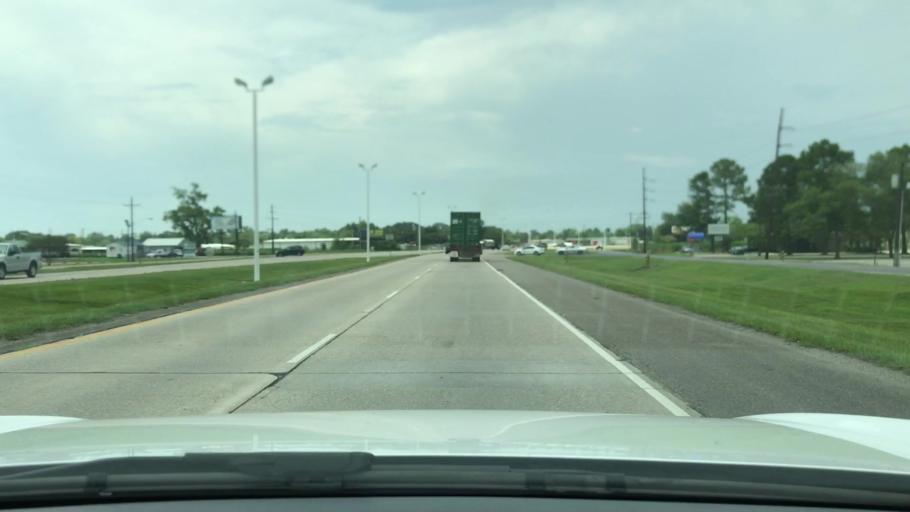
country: US
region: Louisiana
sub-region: West Baton Rouge Parish
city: Addis
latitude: 30.3593
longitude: -91.2604
